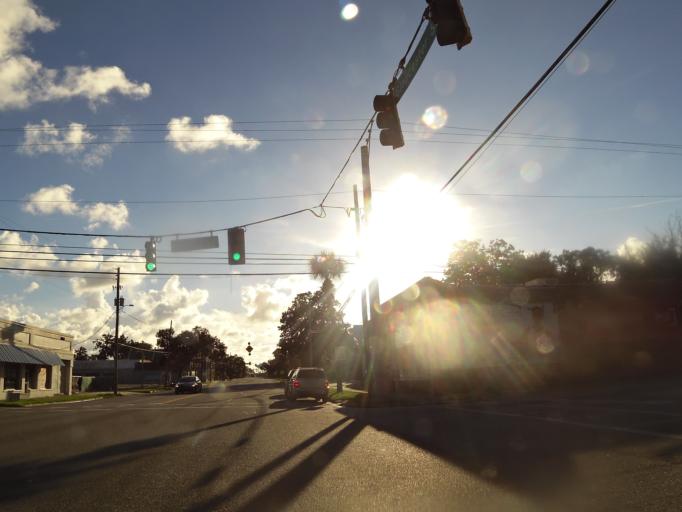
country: US
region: Georgia
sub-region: Glynn County
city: Brunswick
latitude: 31.1508
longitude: -81.4895
